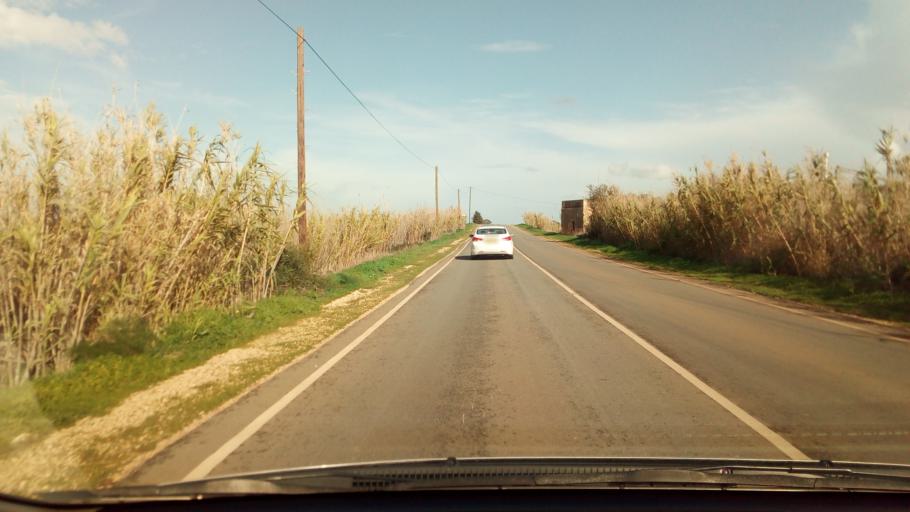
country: CY
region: Ammochostos
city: Achna
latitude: 35.0412
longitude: 33.7667
